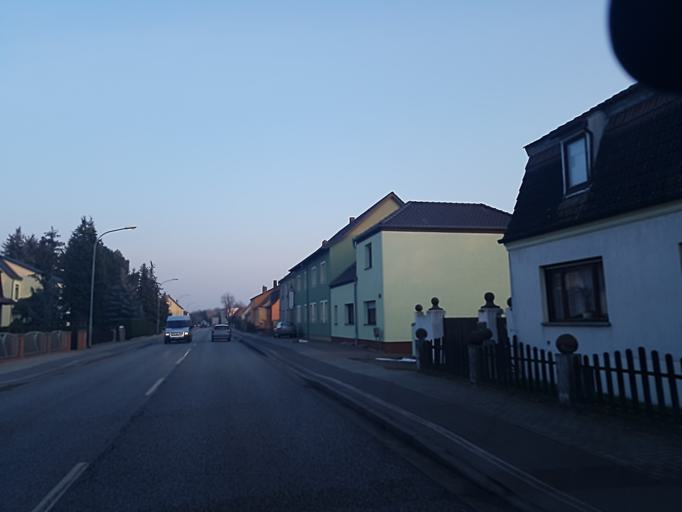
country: DE
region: Saxony-Anhalt
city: Muhlanger
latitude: 51.8583
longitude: 12.7325
